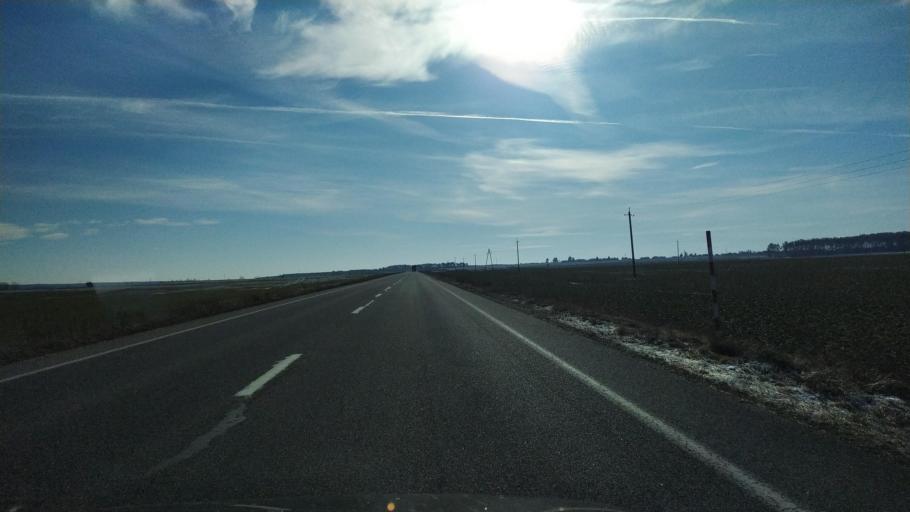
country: BY
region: Brest
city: Kamyanyets
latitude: 52.4187
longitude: 23.8451
